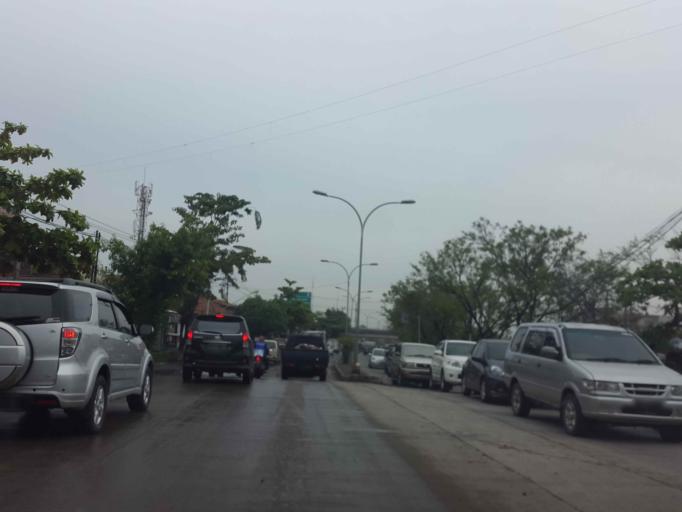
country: ID
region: Central Java
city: Semarang
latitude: -6.9575
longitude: 110.4491
